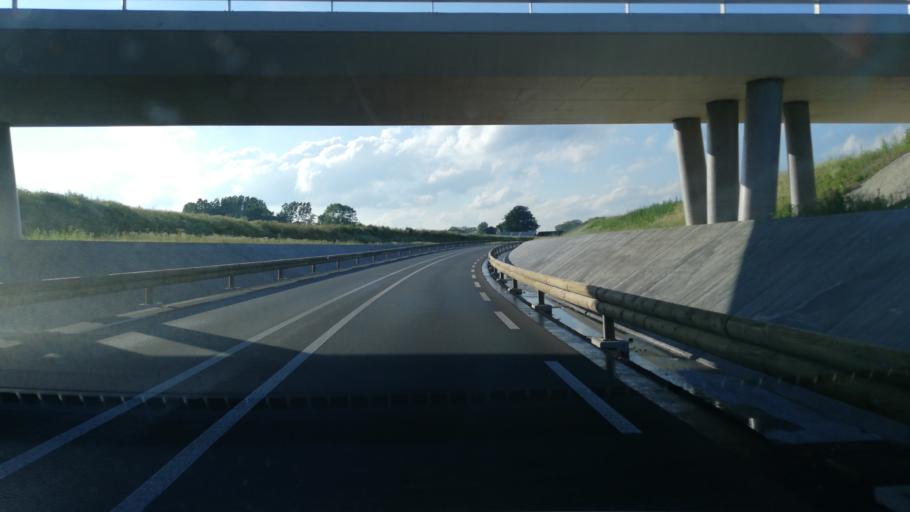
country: NL
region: Gelderland
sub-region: Gemeente Voorst
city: Voorst
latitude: 52.1667
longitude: 6.1339
